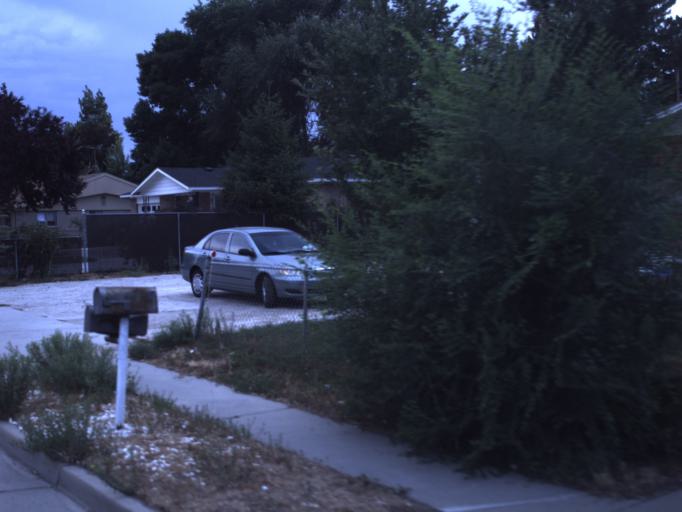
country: US
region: Utah
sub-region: Salt Lake County
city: Millcreek
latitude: 40.6969
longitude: -111.8715
